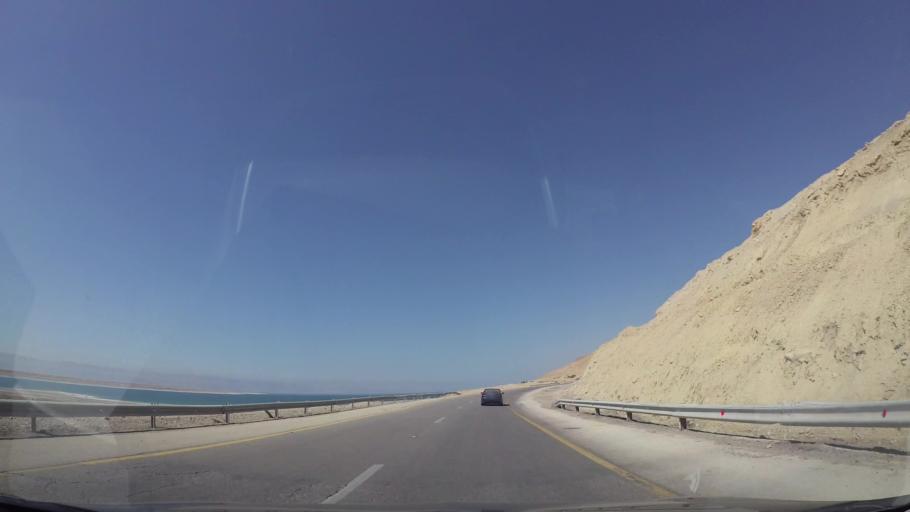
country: JO
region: Karak
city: Al Qasr
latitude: 31.3355
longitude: 35.5481
